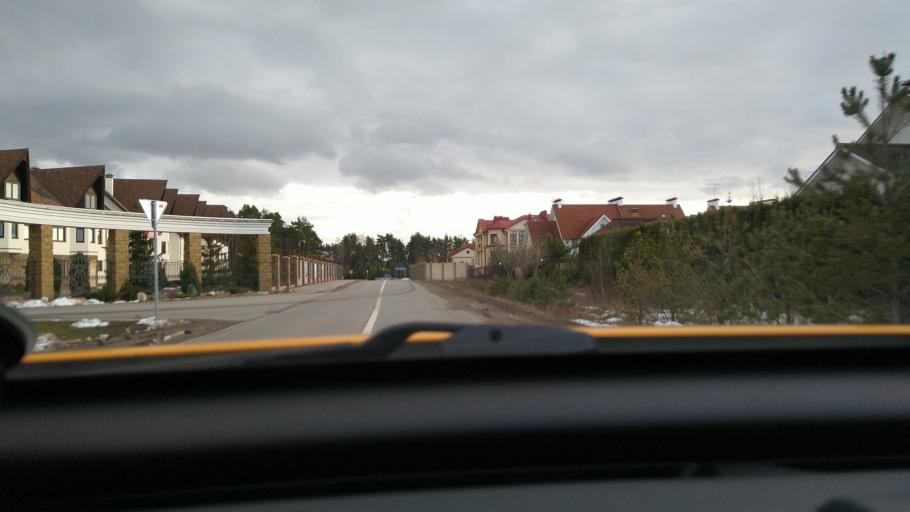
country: RU
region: Moskovskaya
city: Petrovo-Dal'neye
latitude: 55.7509
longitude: 37.2005
